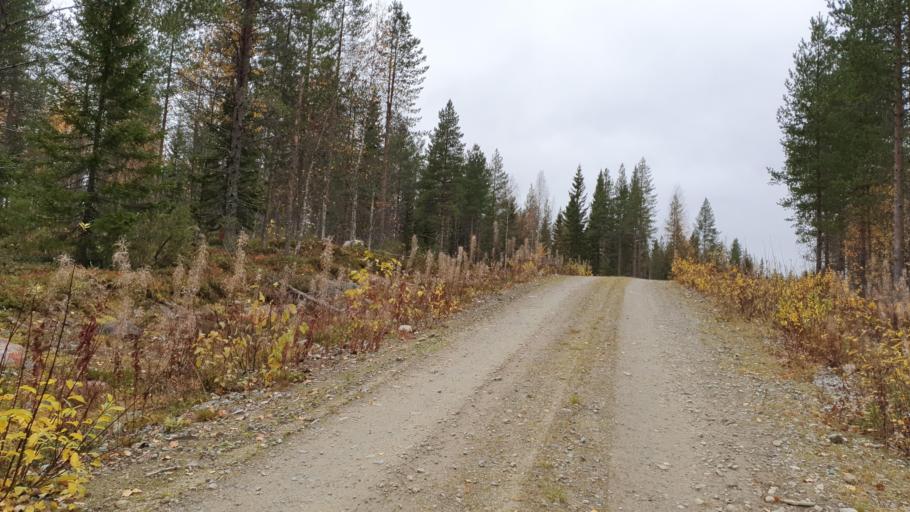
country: FI
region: Kainuu
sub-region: Kehys-Kainuu
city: Kuhmo
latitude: 64.4449
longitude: 29.6375
